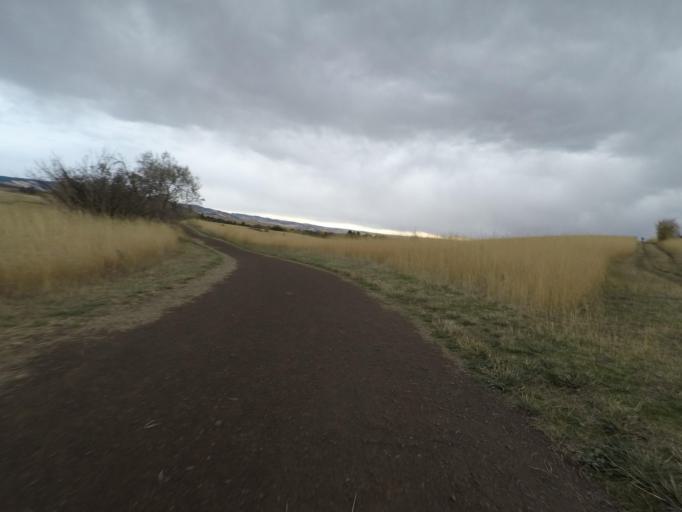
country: US
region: Washington
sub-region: Walla Walla County
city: Walla Walla East
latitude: 46.0720
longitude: -118.2581
